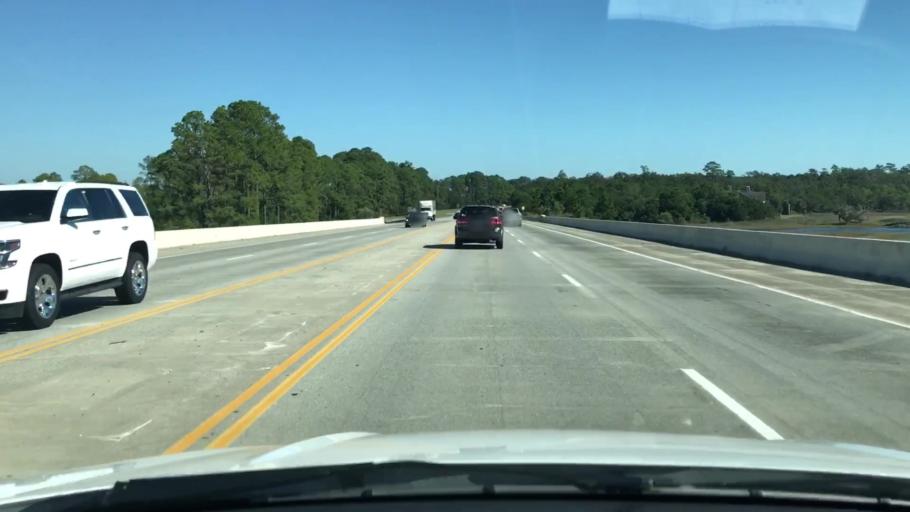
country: US
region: South Carolina
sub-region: Beaufort County
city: Laurel Bay
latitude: 32.3744
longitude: -80.8332
